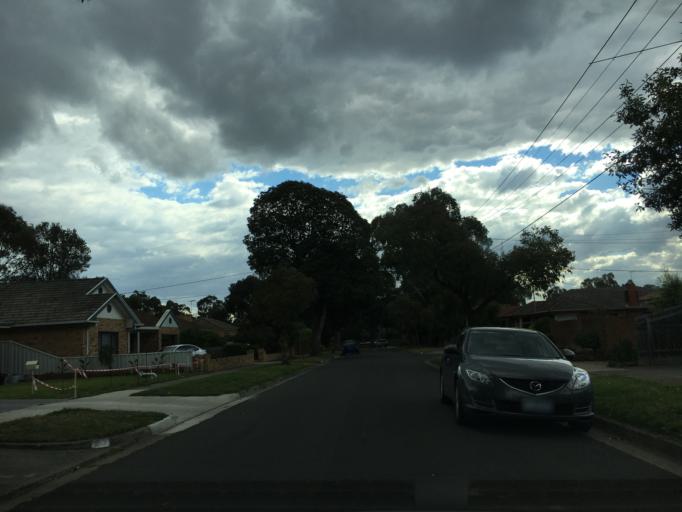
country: AU
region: Victoria
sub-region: Monash
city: Oakleigh South
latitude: -37.9139
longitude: 145.0954
